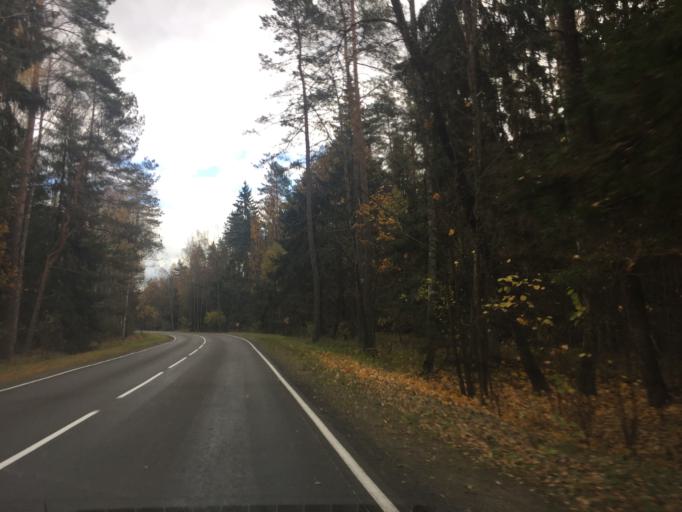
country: BY
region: Minsk
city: Svir
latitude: 54.9230
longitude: 26.5084
